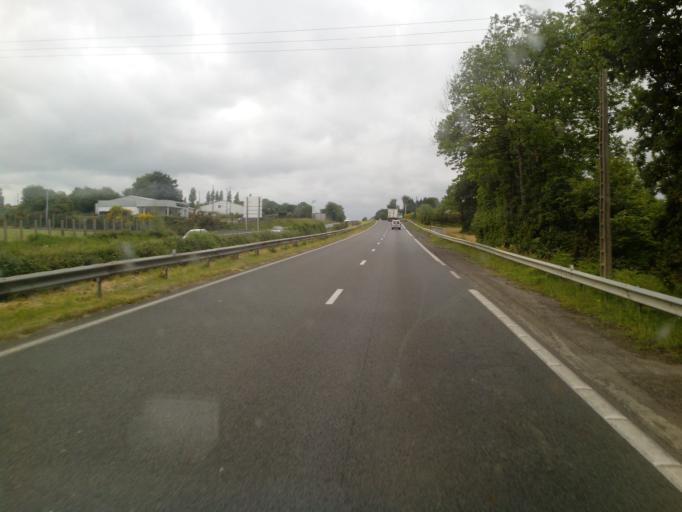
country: FR
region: Brittany
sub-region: Departement des Cotes-d'Armor
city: Graces
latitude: 48.5666
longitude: -3.2236
